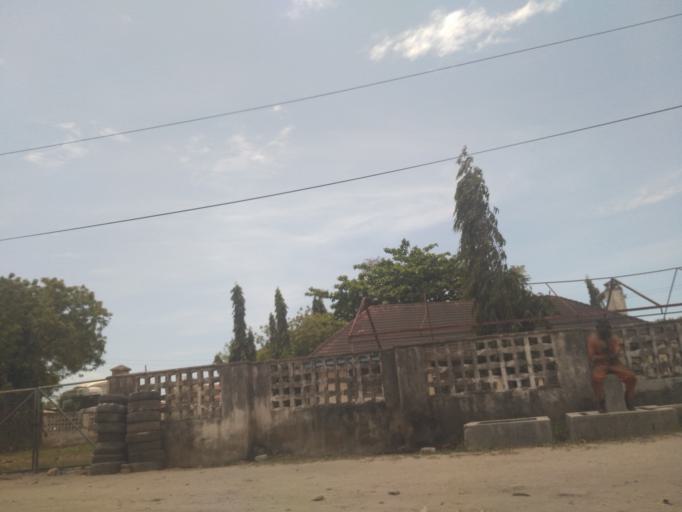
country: TZ
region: Dar es Salaam
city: Dar es Salaam
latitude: -6.8376
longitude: 39.2847
